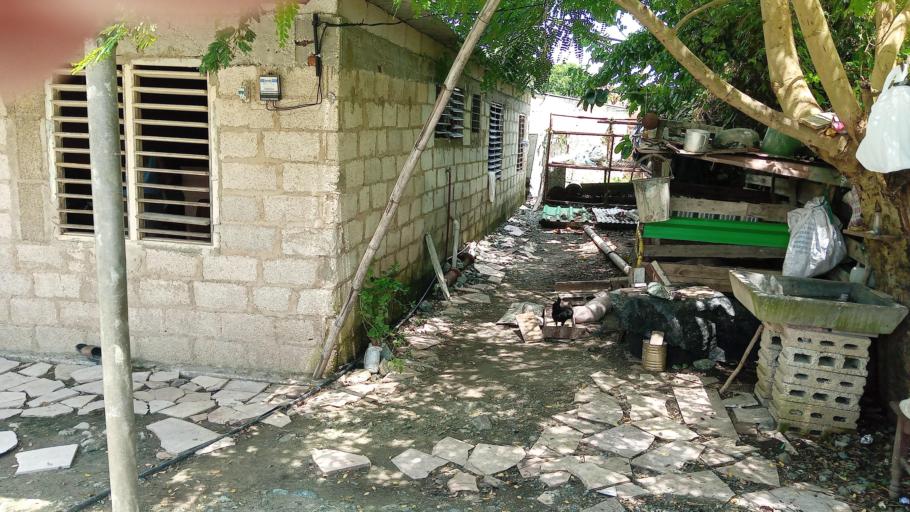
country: CU
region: Villa Clara
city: Santa Clara
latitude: 22.3858
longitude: -79.9457
